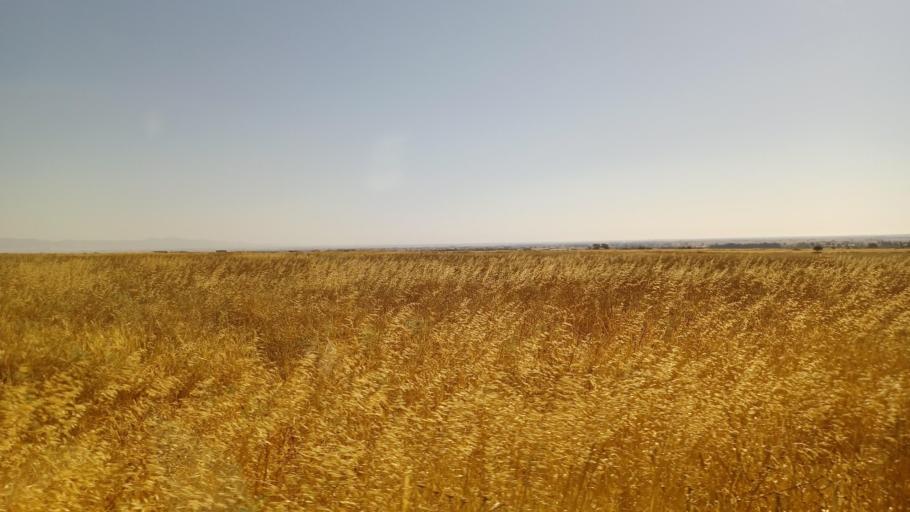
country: CY
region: Larnaka
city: Pergamos
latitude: 35.0433
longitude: 33.6804
